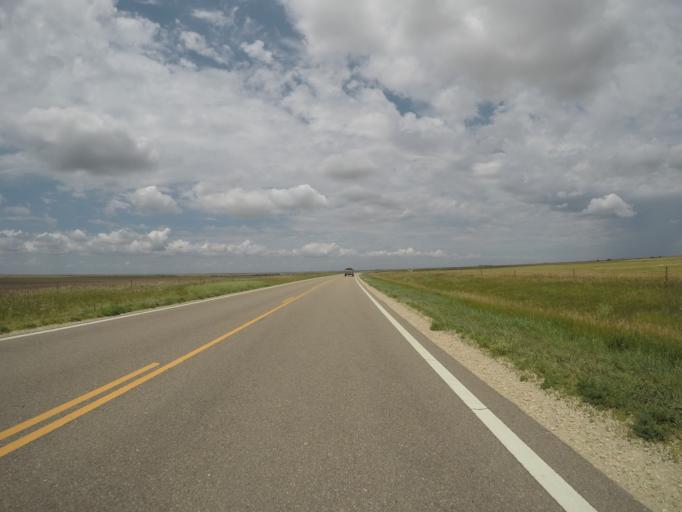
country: US
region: Kansas
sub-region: Rawlins County
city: Atwood
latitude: 39.7311
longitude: -101.0563
